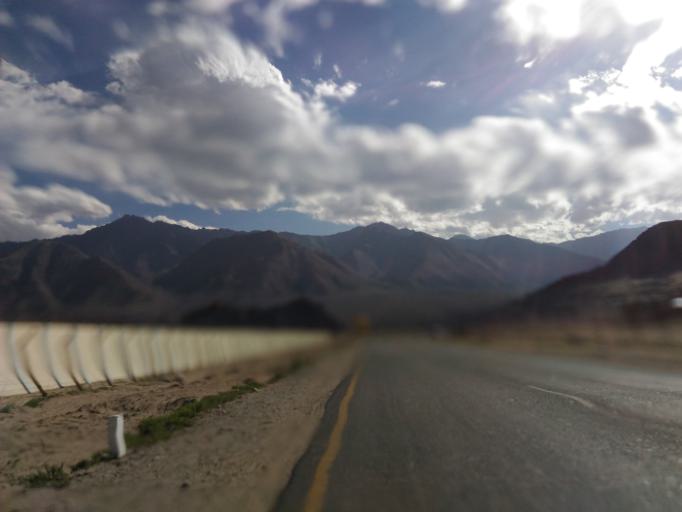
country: IN
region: Kashmir
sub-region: Ladakh
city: Leh
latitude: 34.1354
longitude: 77.5347
